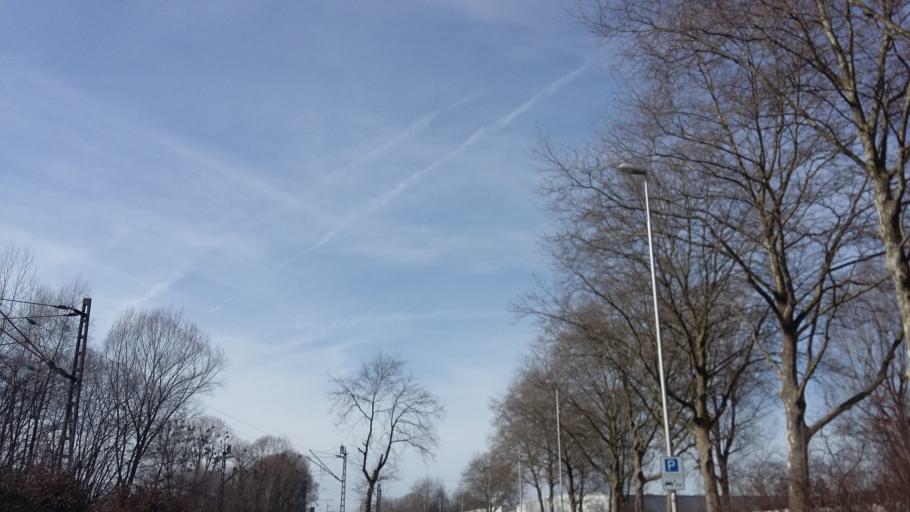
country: AT
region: Vorarlberg
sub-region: Politischer Bezirk Bregenz
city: Horbranz
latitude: 47.5511
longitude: 9.7185
